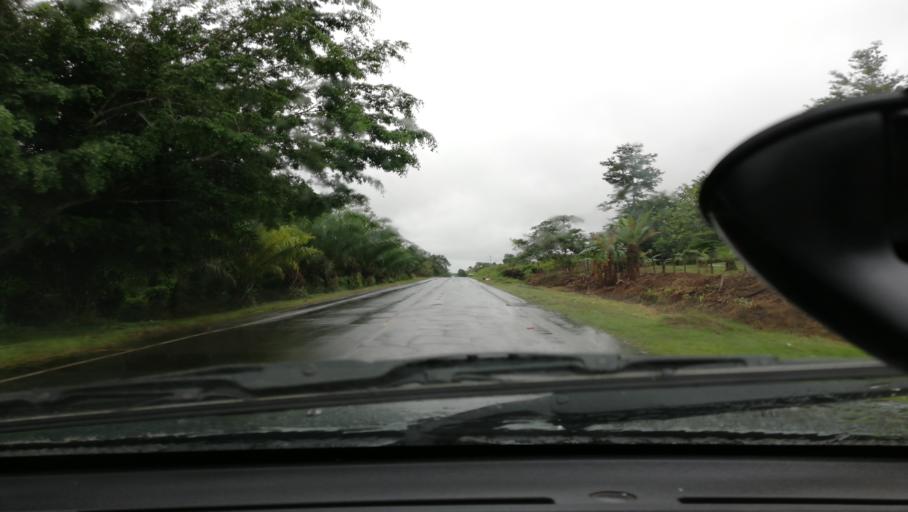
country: PE
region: Loreto
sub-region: Provincia de Maynas
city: San Juan
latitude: -4.0566
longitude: -73.4393
